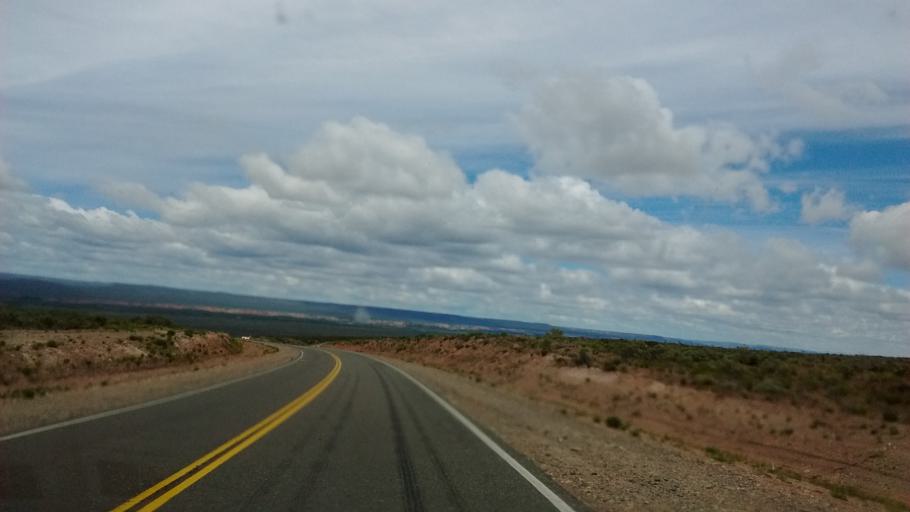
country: AR
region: Neuquen
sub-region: Departamento de Picun Leufu
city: Picun Leufu
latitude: -39.7621
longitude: -69.6493
